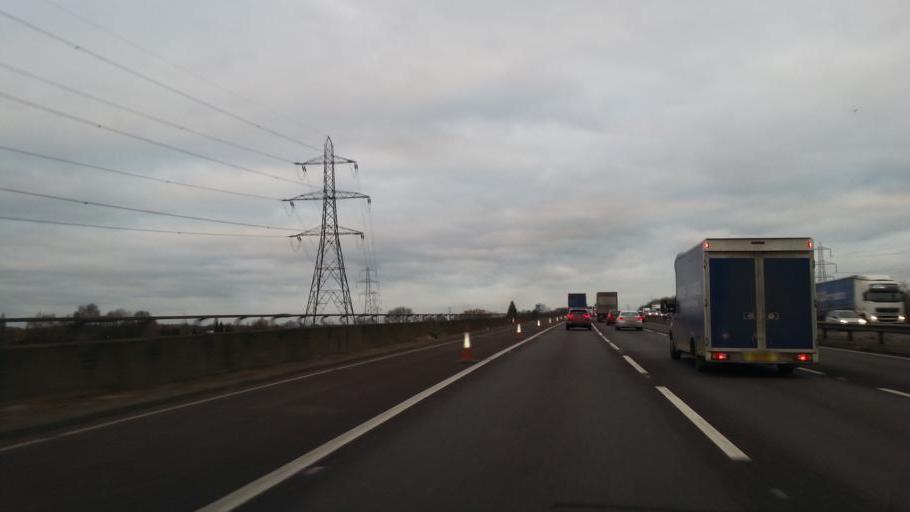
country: GB
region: England
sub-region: Warwickshire
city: Exhall
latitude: 52.4565
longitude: -1.4800
